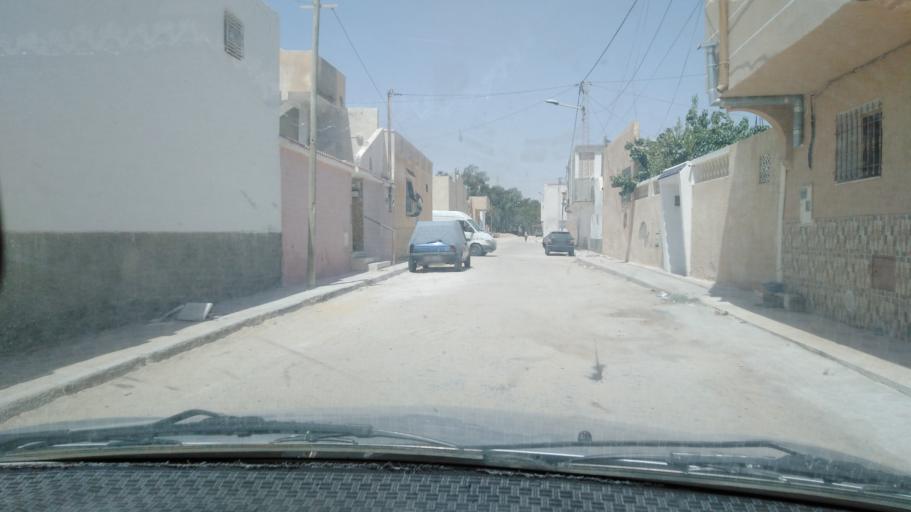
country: TN
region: Qabis
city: Gabes
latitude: 33.9559
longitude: 9.9943
